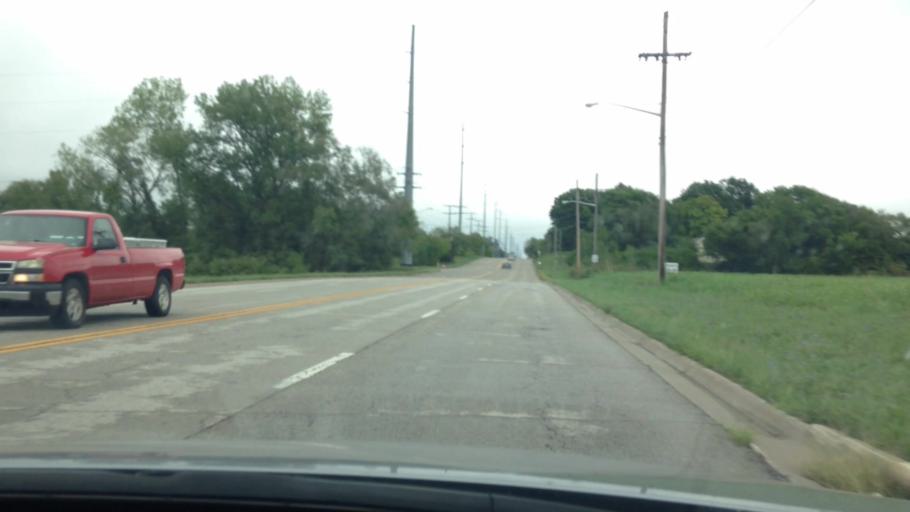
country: US
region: Kansas
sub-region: Wyandotte County
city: Bonner Springs
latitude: 39.1286
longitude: -94.8661
